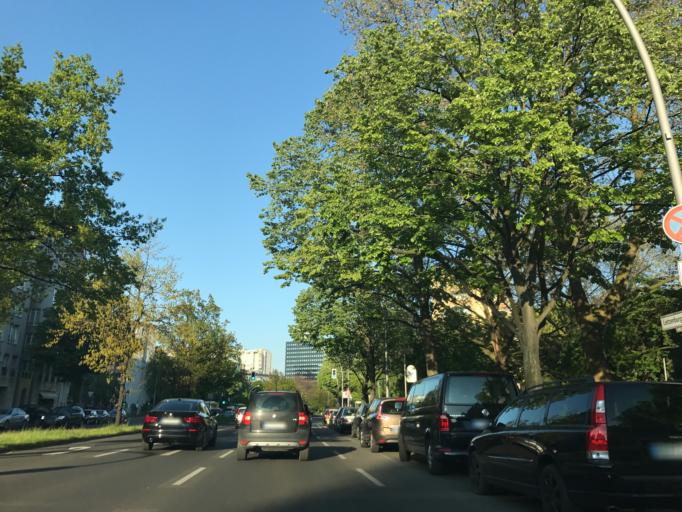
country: DE
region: Berlin
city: Berlin Schoeneberg
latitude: 52.4996
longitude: 13.3396
